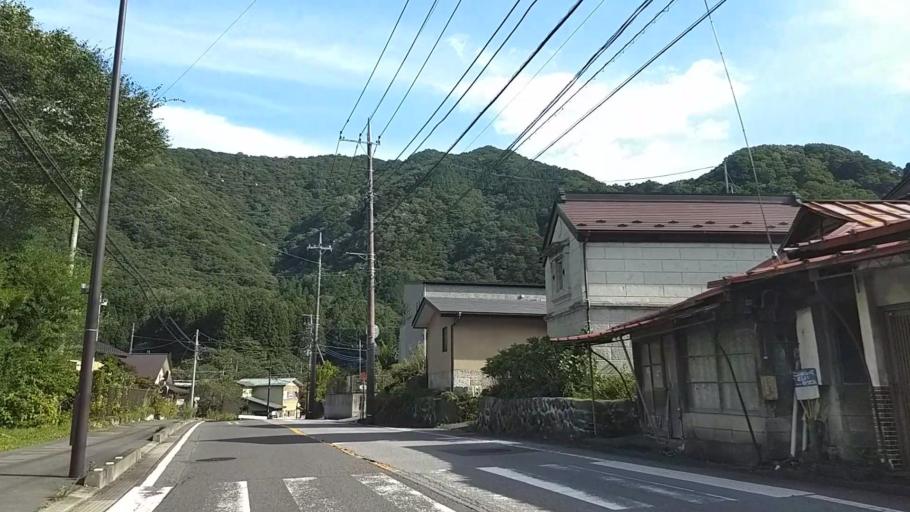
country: JP
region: Tochigi
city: Imaichi
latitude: 36.8527
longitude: 139.7320
